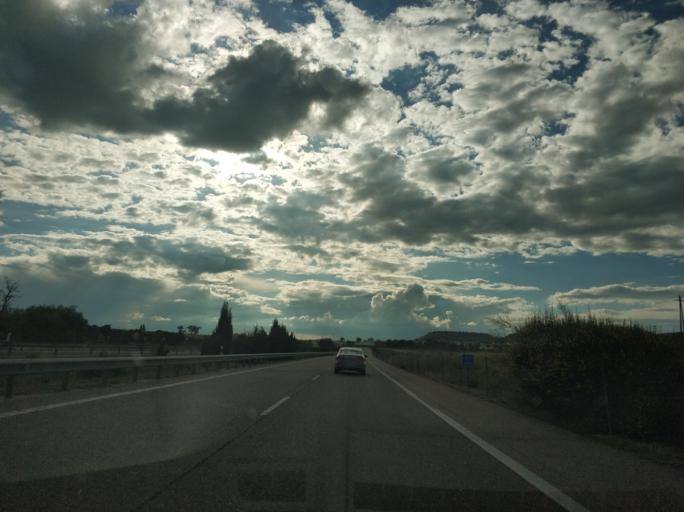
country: ES
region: Castille and Leon
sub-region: Provincia de Valladolid
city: Tudela de Duero
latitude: 41.5945
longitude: -4.6203
